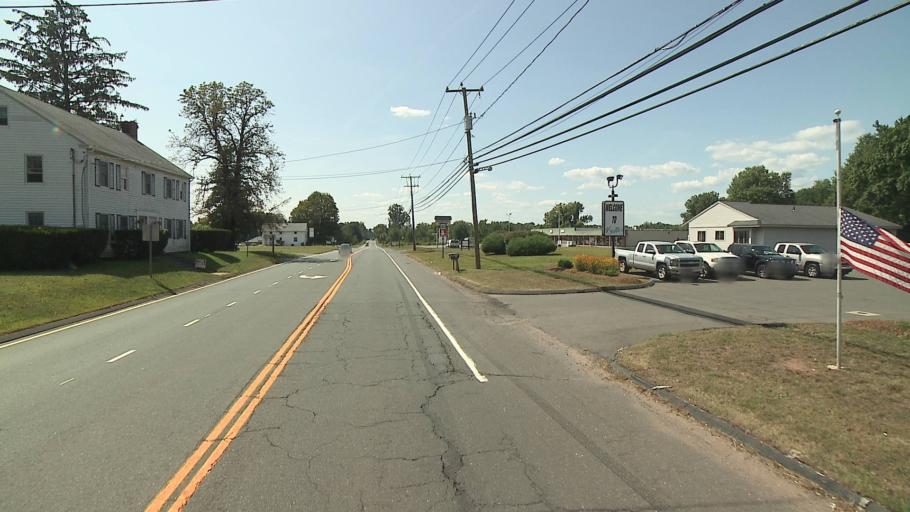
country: US
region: Connecticut
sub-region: Hartford County
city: Southwood Acres
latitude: 41.9361
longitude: -72.5770
